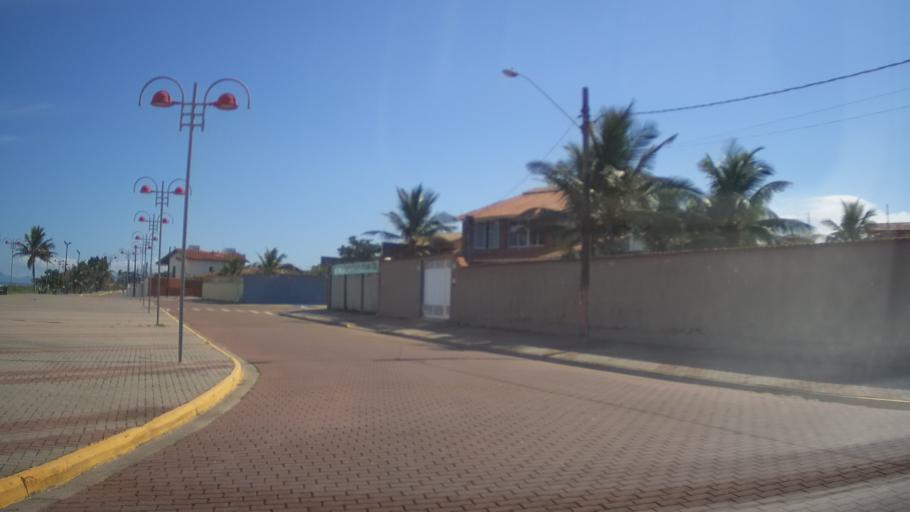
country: BR
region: Sao Paulo
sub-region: Itanhaem
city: Itanhaem
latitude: -24.1728
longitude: -46.7628
